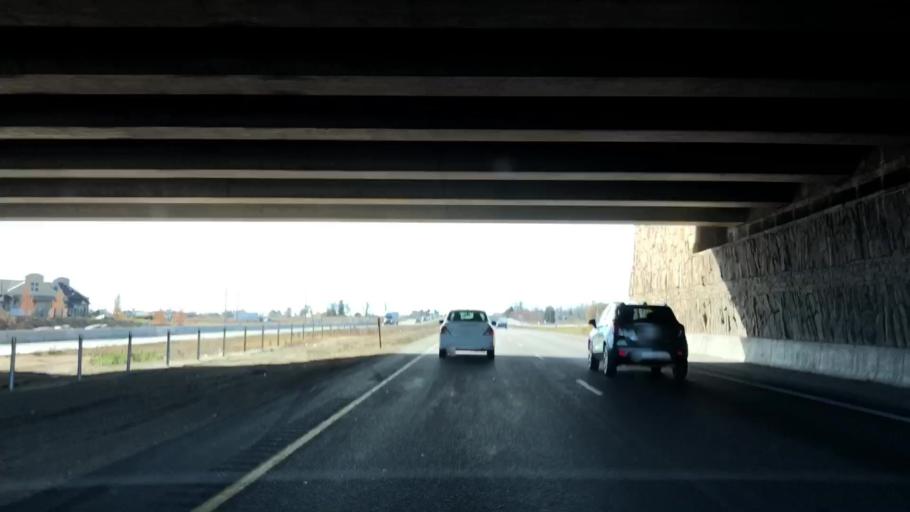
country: US
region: Colorado
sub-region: Weld County
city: Windsor
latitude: 40.4794
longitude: -104.9900
